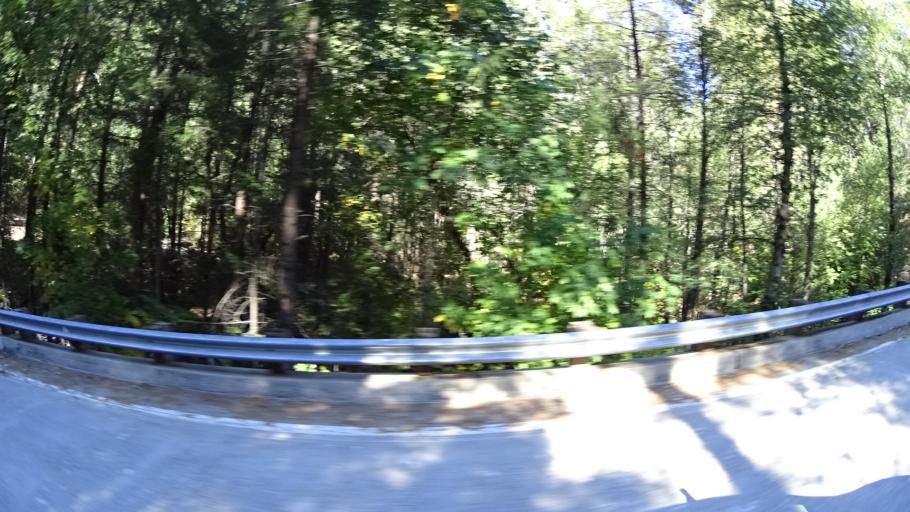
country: US
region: California
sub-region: Trinity County
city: Weaverville
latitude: 41.2032
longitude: -123.0714
